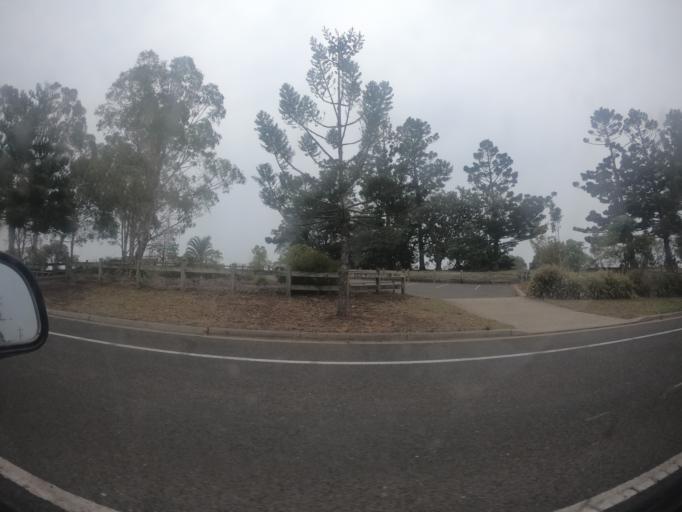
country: AU
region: New South Wales
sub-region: Shellharbour
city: Croom
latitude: -34.5726
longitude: 150.8315
